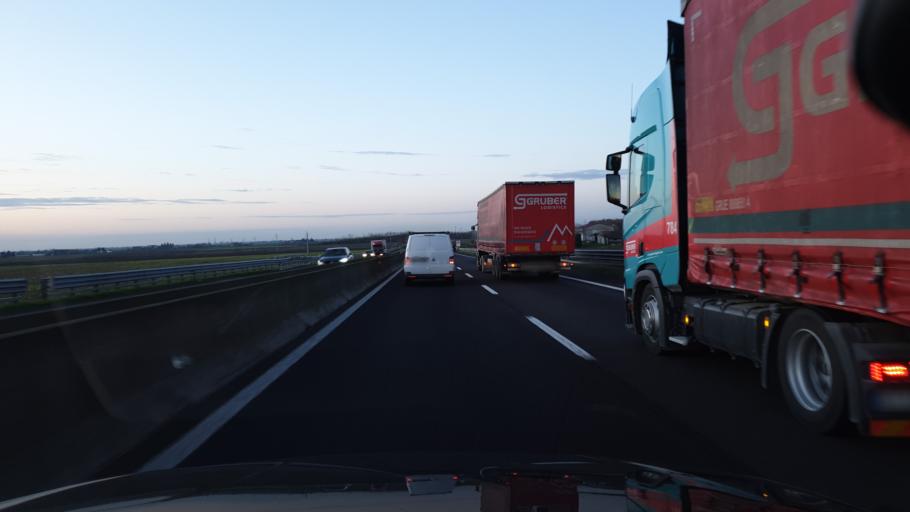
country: IT
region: Veneto
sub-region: Provincia di Rovigo
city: Villamarzana
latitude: 45.0037
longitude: 11.6776
